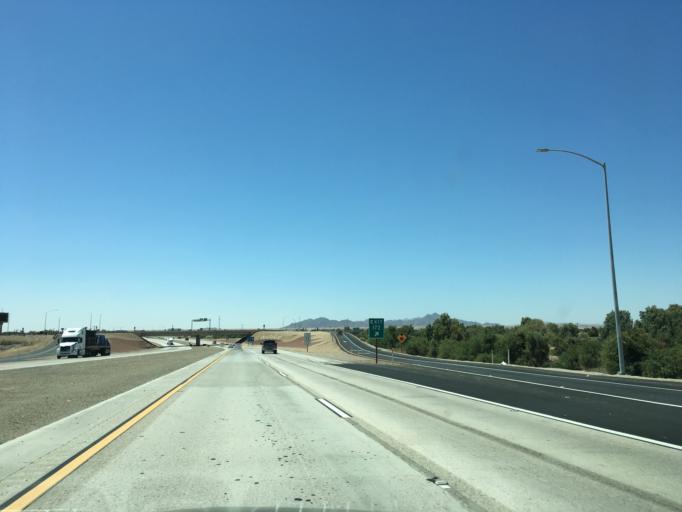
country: US
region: Arizona
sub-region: Yuma County
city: Yuma
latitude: 32.7303
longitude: -114.6210
